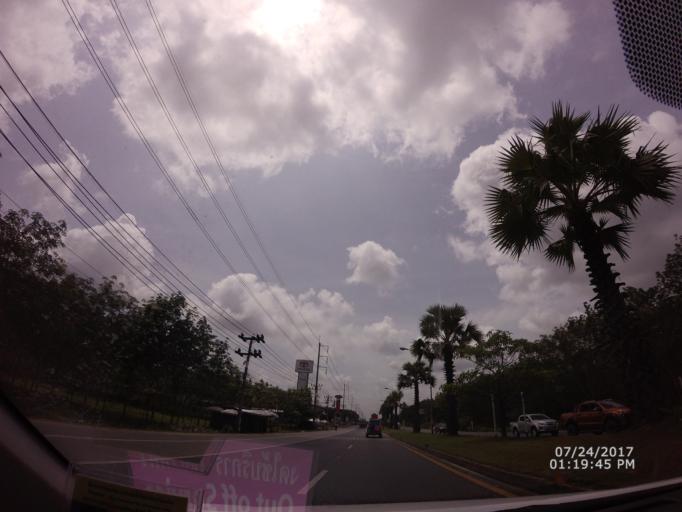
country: TH
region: Phuket
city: Thalang
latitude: 8.0616
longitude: 98.3409
